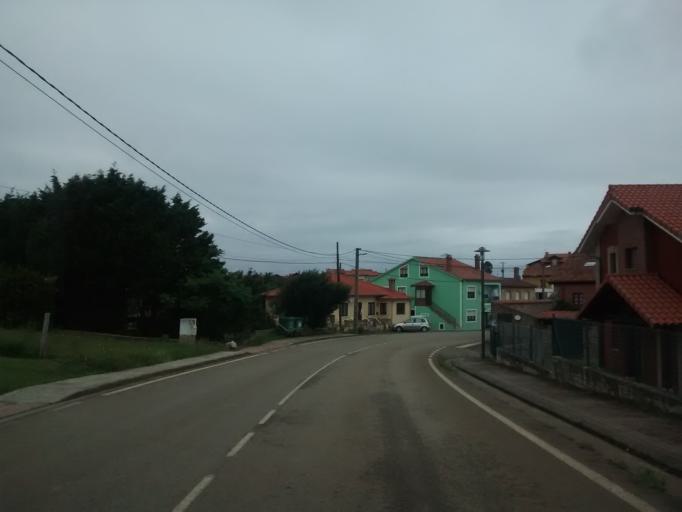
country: ES
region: Cantabria
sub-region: Provincia de Cantabria
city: Santillana
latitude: 43.4167
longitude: -4.1000
